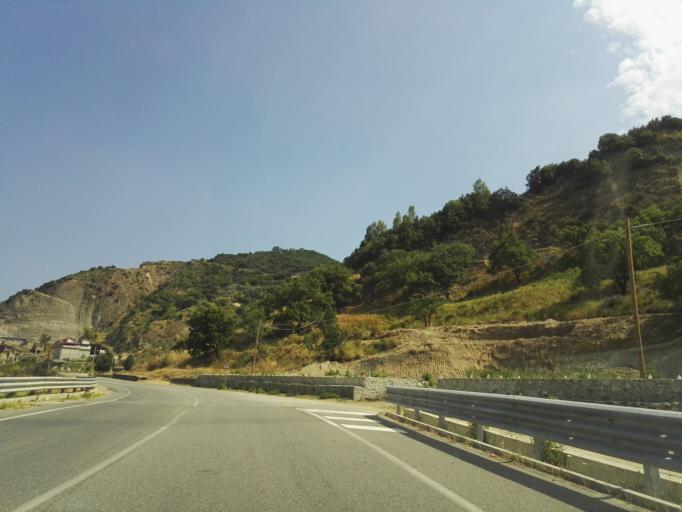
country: IT
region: Calabria
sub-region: Provincia di Reggio Calabria
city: Stilo
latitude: 38.4669
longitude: 16.4855
